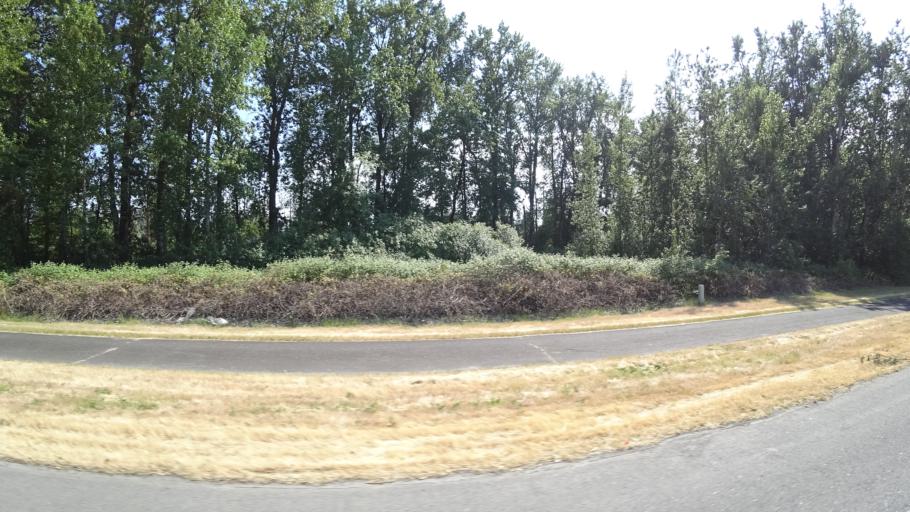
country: US
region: Oregon
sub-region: Multnomah County
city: Fairview
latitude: 45.5561
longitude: -122.4291
